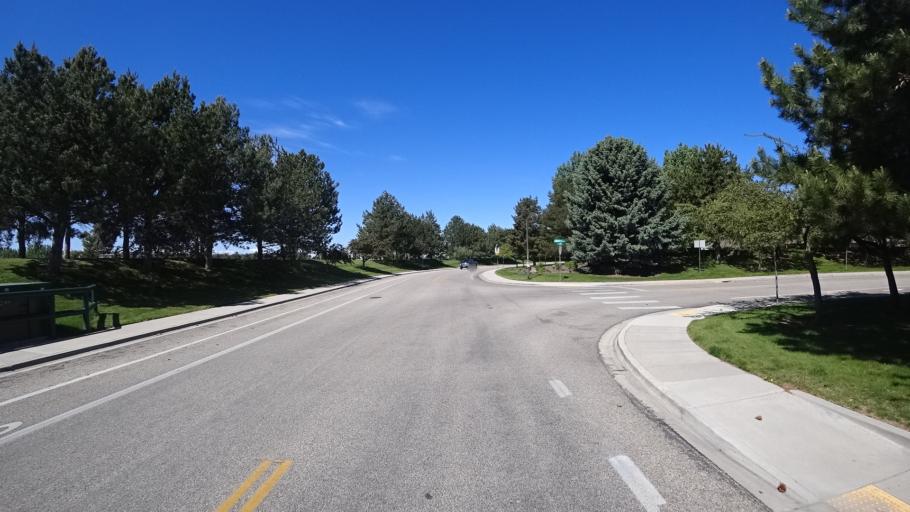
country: US
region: Idaho
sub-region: Ada County
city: Boise
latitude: 43.5500
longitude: -116.1442
